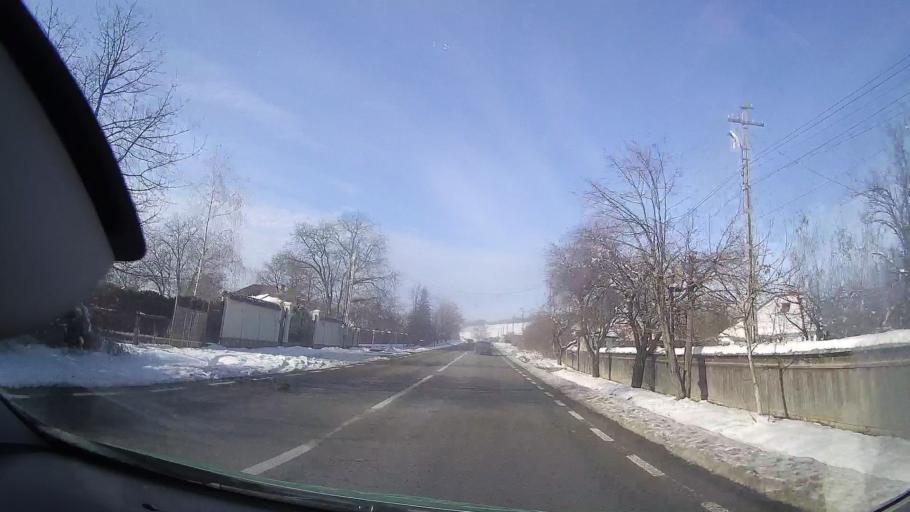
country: RO
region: Neamt
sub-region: Comuna Dobreni
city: Dobreni
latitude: 46.9961
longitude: 26.3909
